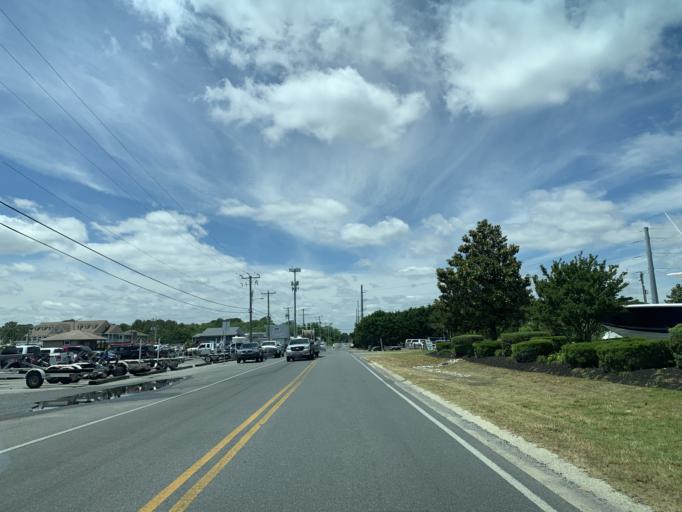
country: US
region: Maryland
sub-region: Worcester County
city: West Ocean City
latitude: 38.3279
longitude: -75.1057
